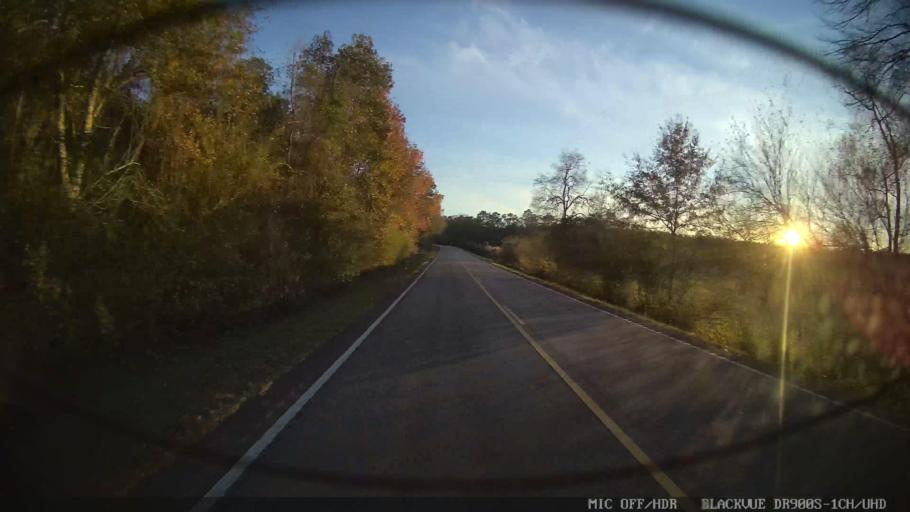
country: US
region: Mississippi
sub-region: Stone County
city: Wiggins
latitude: 31.0123
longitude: -89.2561
